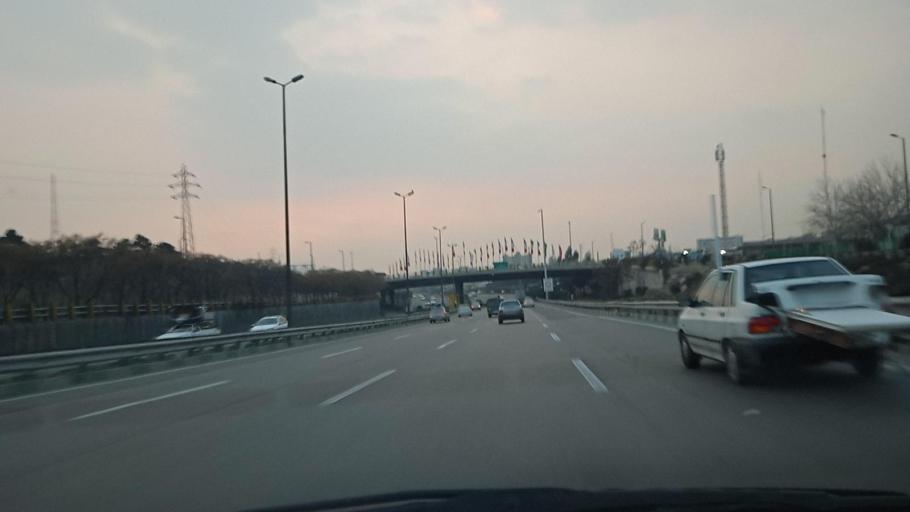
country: IR
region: Tehran
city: Tehran
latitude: 35.7221
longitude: 51.5249
